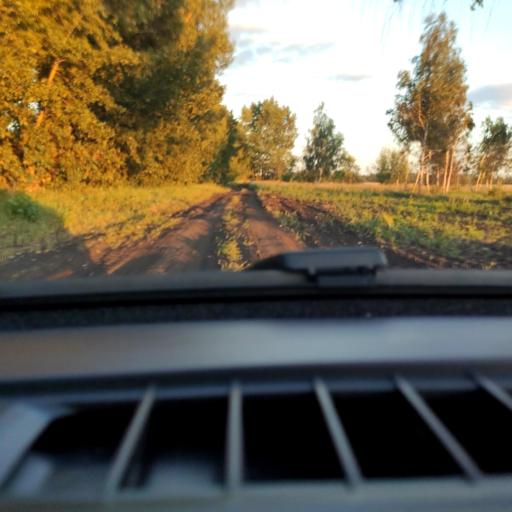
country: RU
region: Voronezj
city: Panino
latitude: 51.5717
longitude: 39.8814
